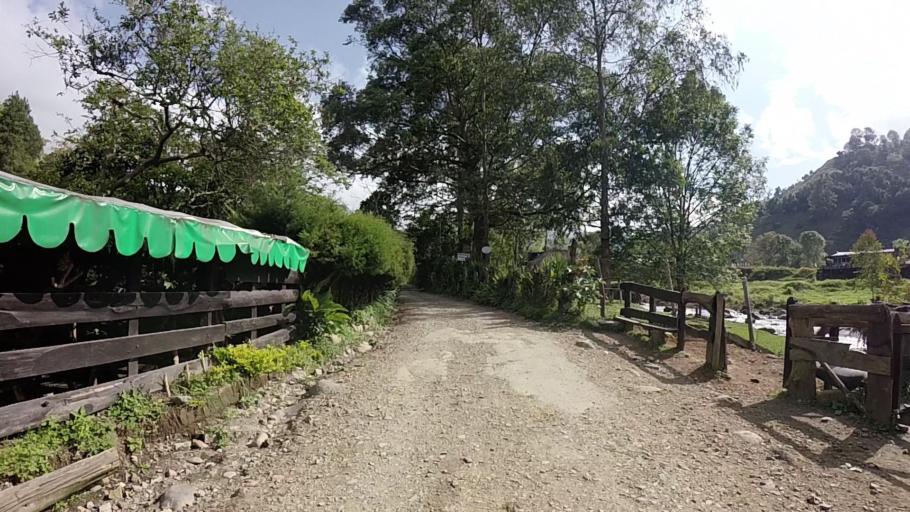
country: CO
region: Quindio
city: Salento
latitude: 4.6434
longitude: -75.5838
